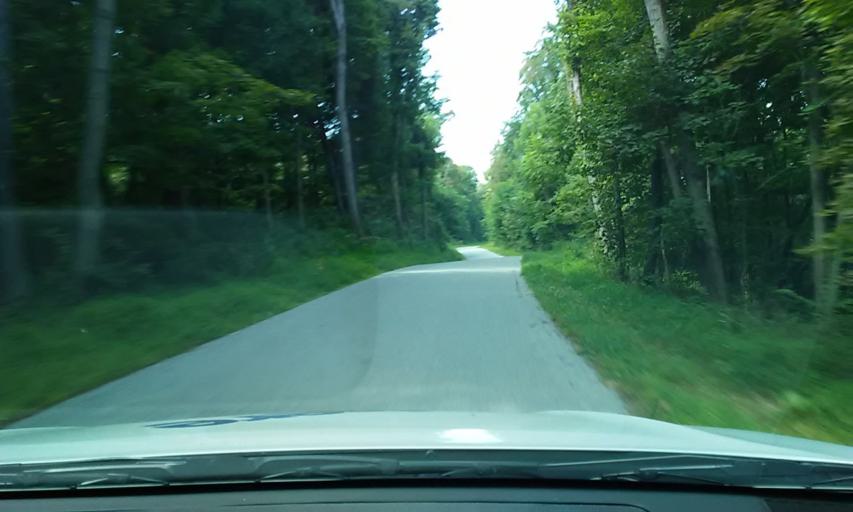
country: US
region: Pennsylvania
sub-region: Fayette County
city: Point Marion
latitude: 39.7410
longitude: -79.9579
